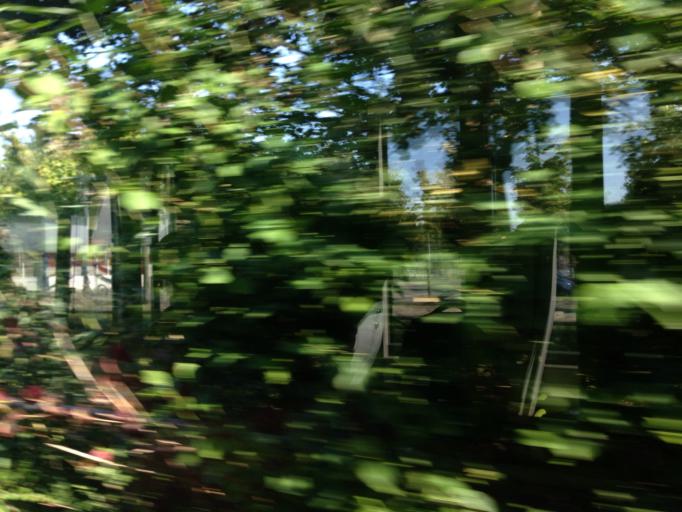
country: NL
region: Flevoland
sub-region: Gemeente Almere
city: Almere Stad
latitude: 52.3684
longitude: 5.2105
